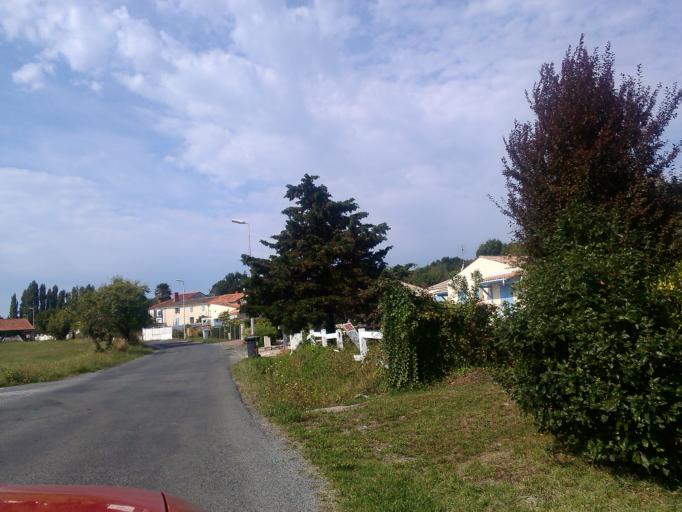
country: FR
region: Poitou-Charentes
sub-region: Departement de la Charente-Maritime
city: Chaillevette
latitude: 45.7246
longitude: -1.0675
